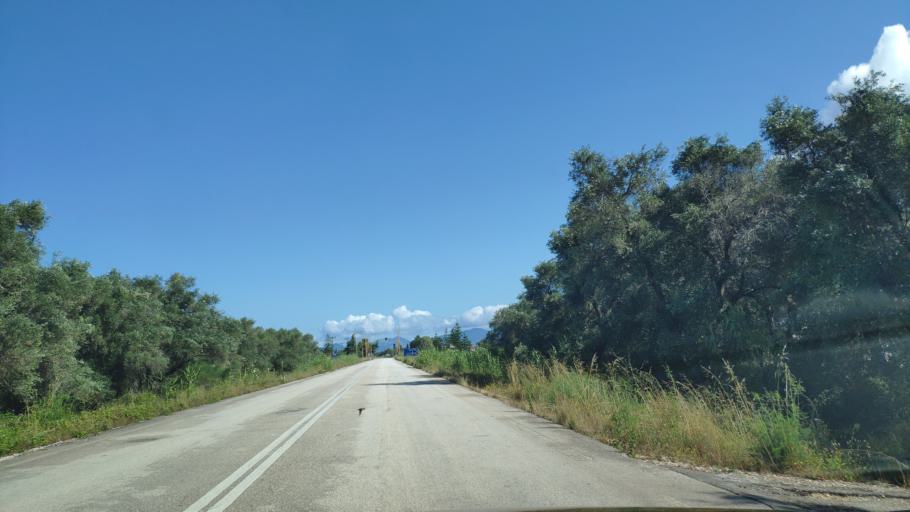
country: GR
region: Epirus
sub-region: Nomos Prevezis
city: Preveza
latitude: 38.9598
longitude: 20.7285
